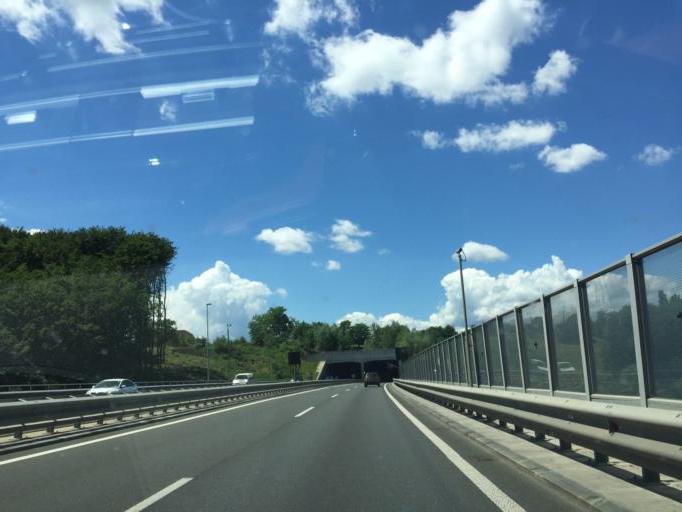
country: SI
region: Sveti Jurij v Slovenskih Goricah
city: Jurovski Dol
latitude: 46.5705
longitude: 15.7723
